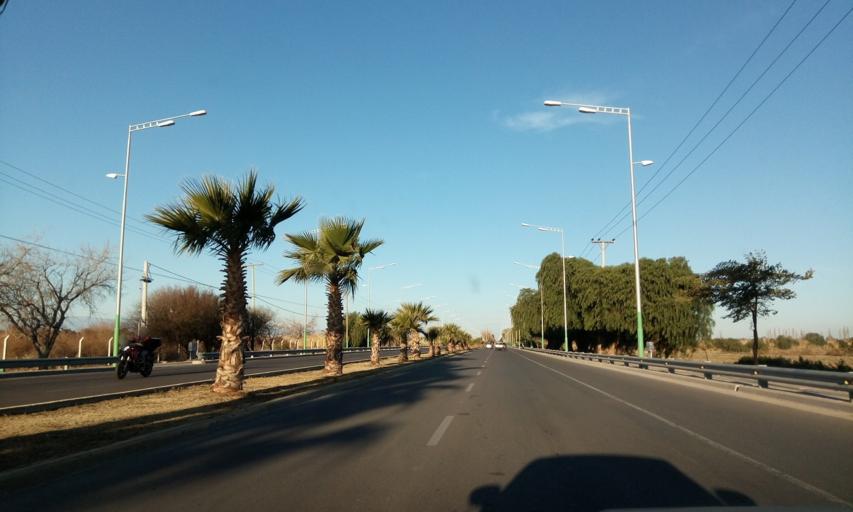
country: AR
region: San Juan
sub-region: Departamento de Rivadavia
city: Rivadavia
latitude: -31.5246
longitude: -68.6145
